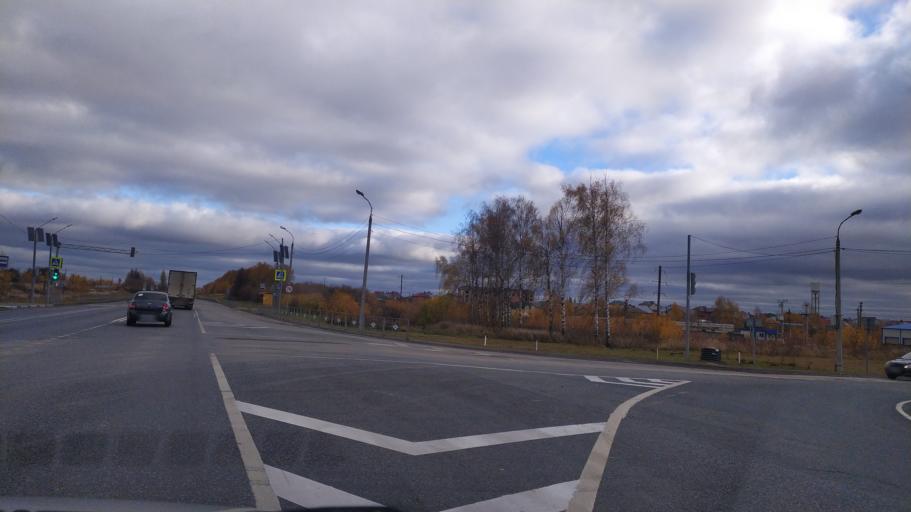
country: RU
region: Chuvashia
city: Novyye Lapsary
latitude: 56.0610
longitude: 47.2505
